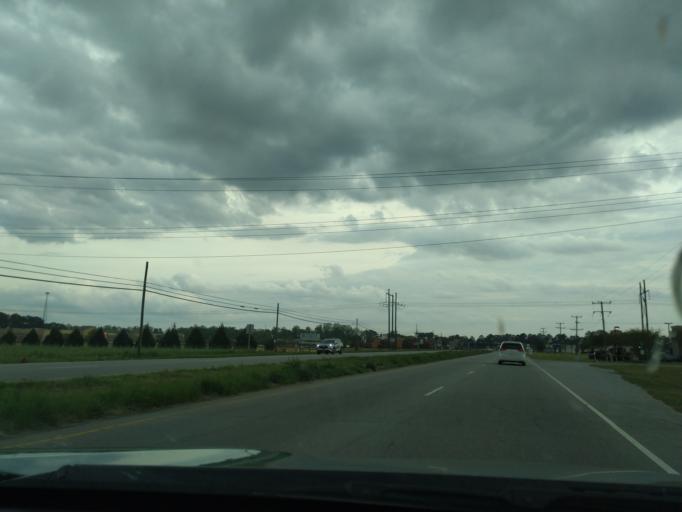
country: US
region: North Carolina
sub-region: Martin County
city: Williamston
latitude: 35.8382
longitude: -77.0651
